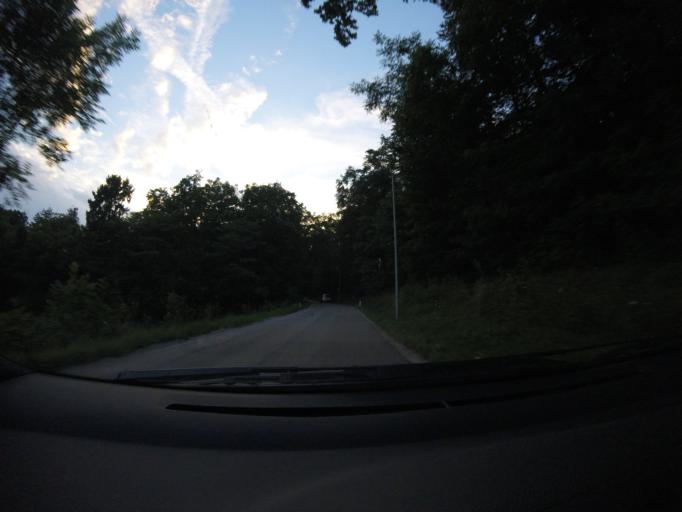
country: AT
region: Styria
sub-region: Politischer Bezirk Graz-Umgebung
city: Hart bei Graz
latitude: 47.0591
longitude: 15.5268
